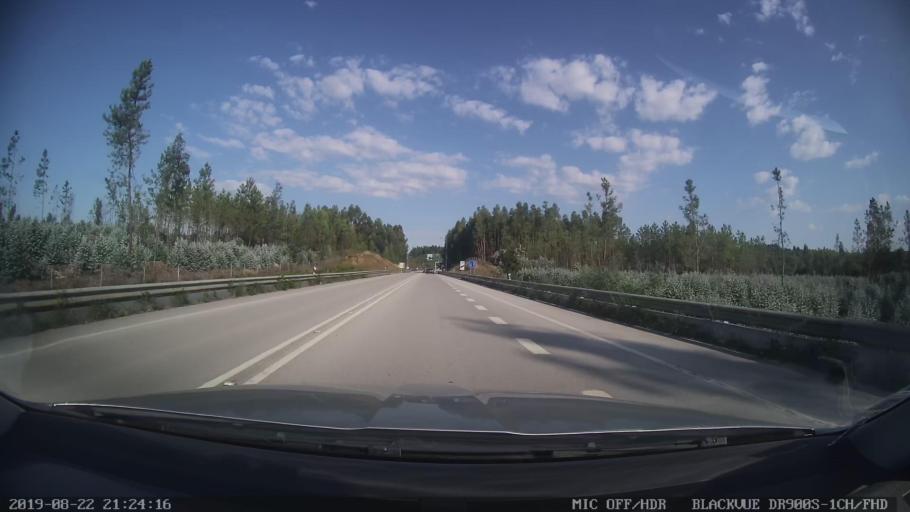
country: PT
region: Castelo Branco
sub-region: Serta
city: Serta
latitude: 39.8396
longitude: -8.1200
